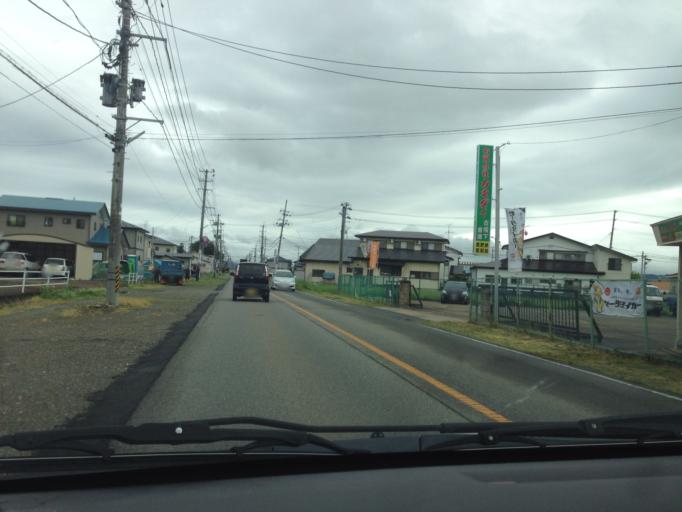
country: JP
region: Fukushima
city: Kitakata
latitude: 37.5584
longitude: 139.8298
